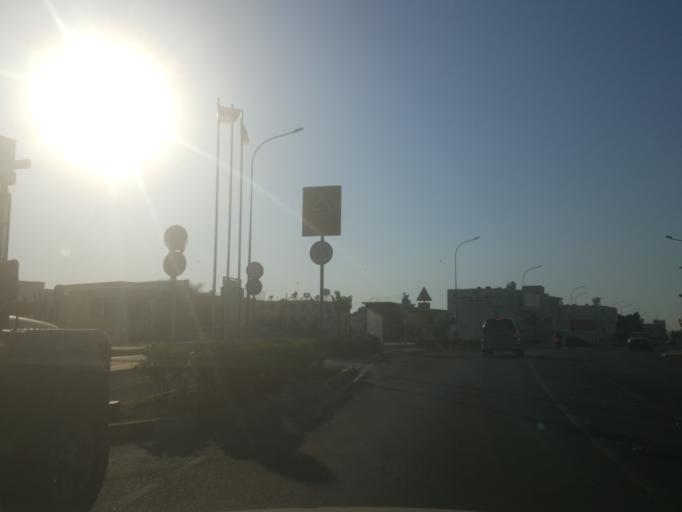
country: CY
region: Ammochostos
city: Deryneia
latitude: 35.0539
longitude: 33.9729
